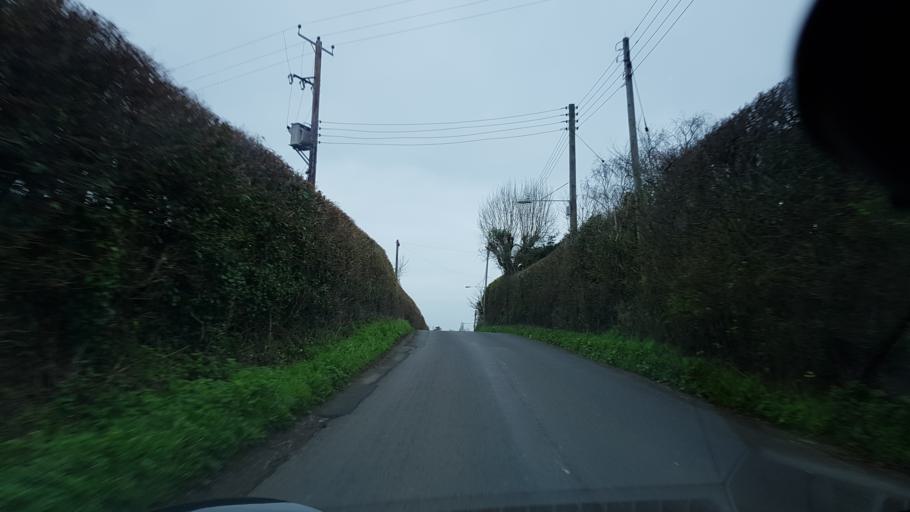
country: GB
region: England
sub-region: Somerset
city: Creech Saint Michael
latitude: 51.0078
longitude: -3.0425
